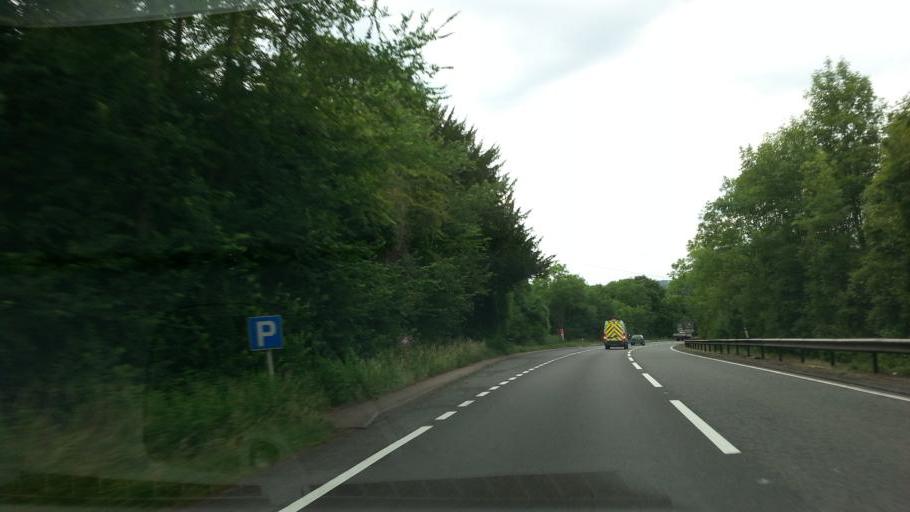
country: GB
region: England
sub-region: Herefordshire
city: Marstow
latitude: 51.8898
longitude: -2.6371
